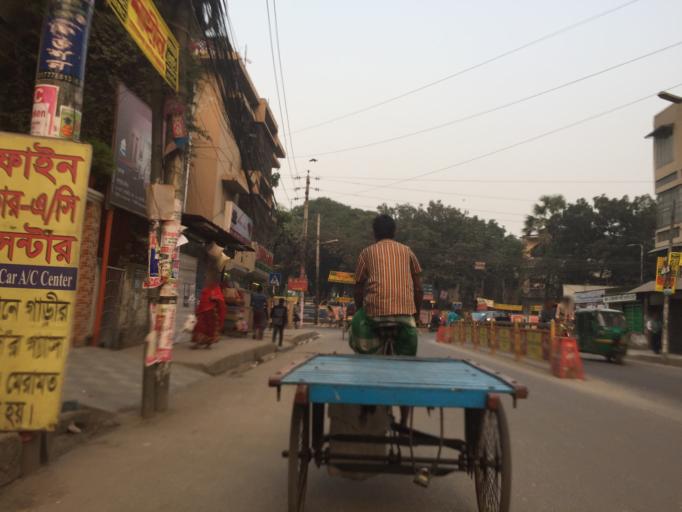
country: BD
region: Dhaka
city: Azimpur
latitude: 23.7642
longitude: 90.3650
